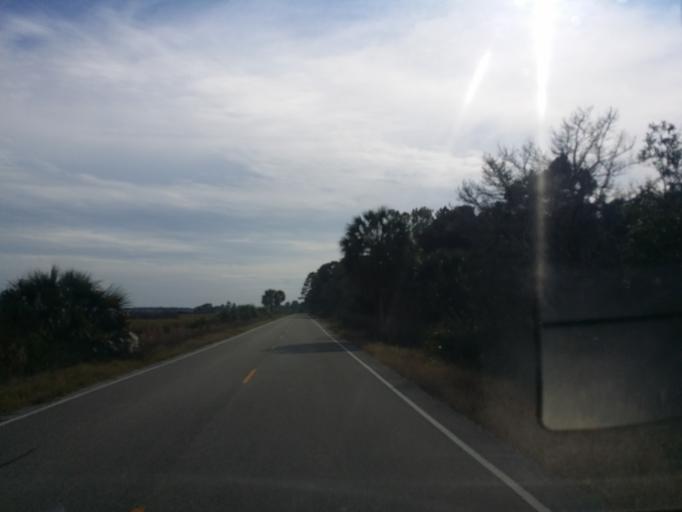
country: US
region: Florida
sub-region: Leon County
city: Woodville
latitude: 30.1149
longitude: -84.1490
